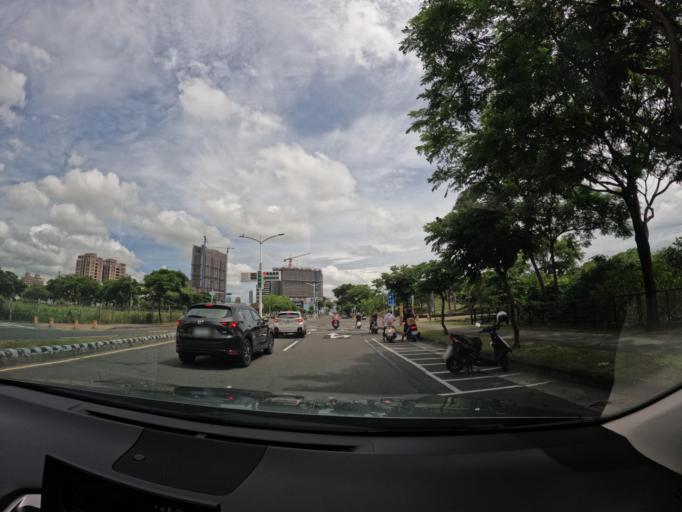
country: TW
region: Kaohsiung
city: Kaohsiung
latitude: 22.6477
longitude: 120.2880
